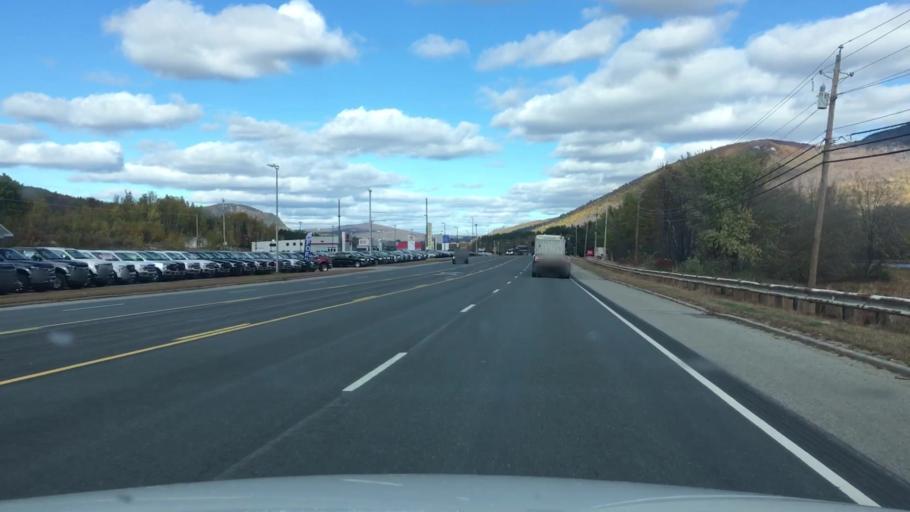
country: US
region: New Hampshire
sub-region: Coos County
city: Gorham
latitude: 44.4104
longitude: -71.1959
